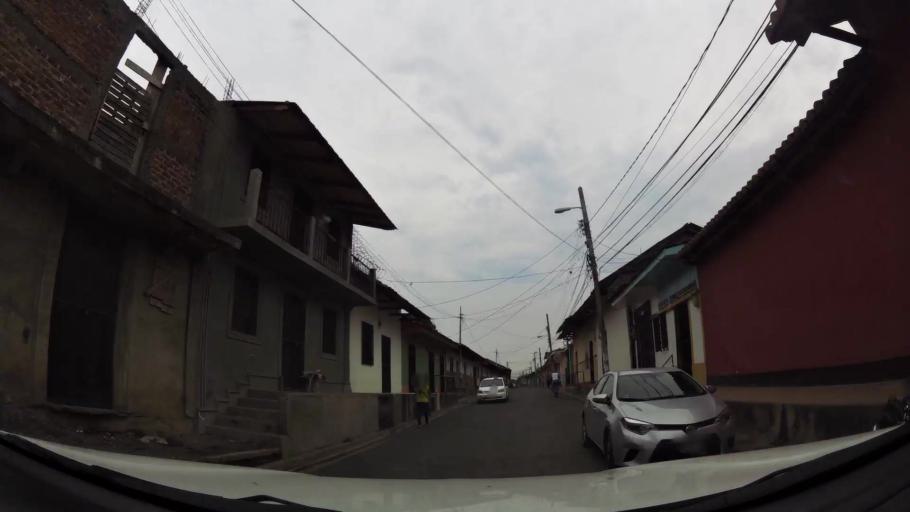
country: NI
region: Granada
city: Granada
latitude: 11.9290
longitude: -85.9504
